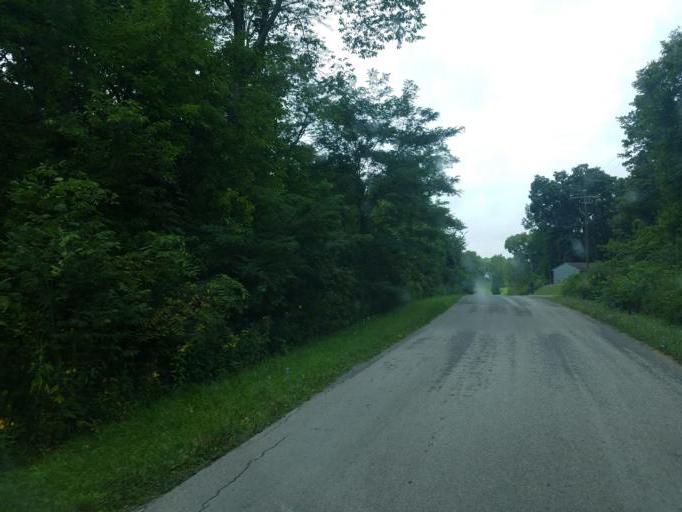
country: US
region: Ohio
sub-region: Morrow County
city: Cardington
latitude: 40.4177
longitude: -82.8501
